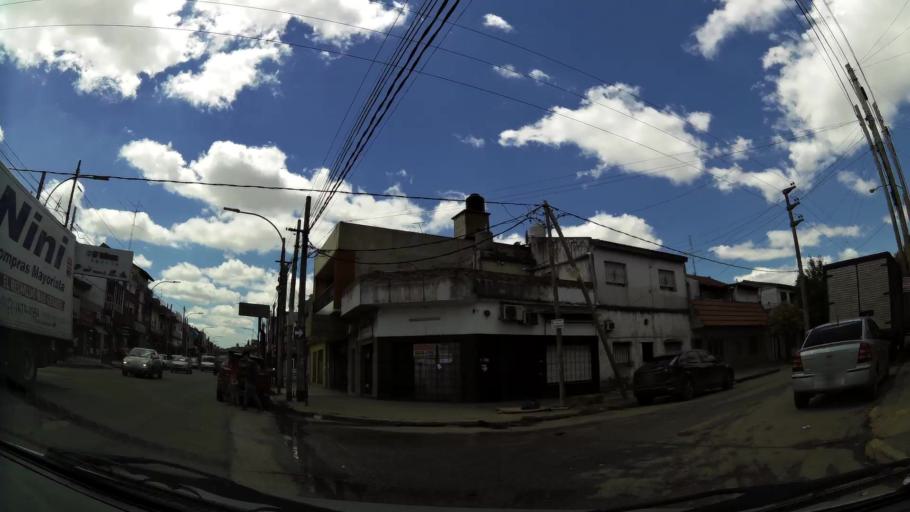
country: AR
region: Buenos Aires
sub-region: Partido de Lanus
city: Lanus
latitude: -34.7098
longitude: -58.4208
